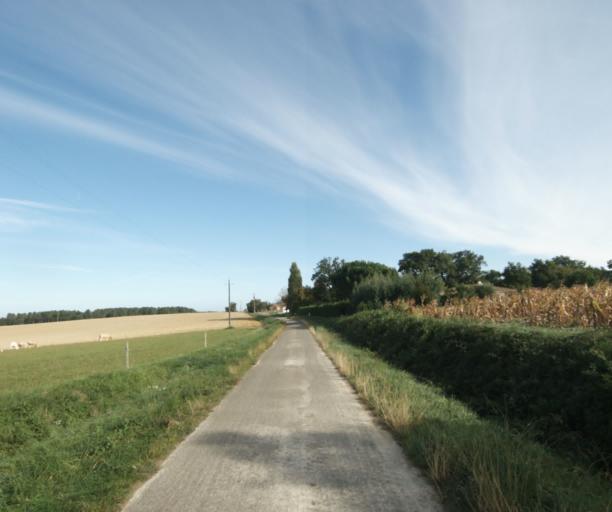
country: FR
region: Midi-Pyrenees
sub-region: Departement du Gers
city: Eauze
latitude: 43.9140
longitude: 0.1199
